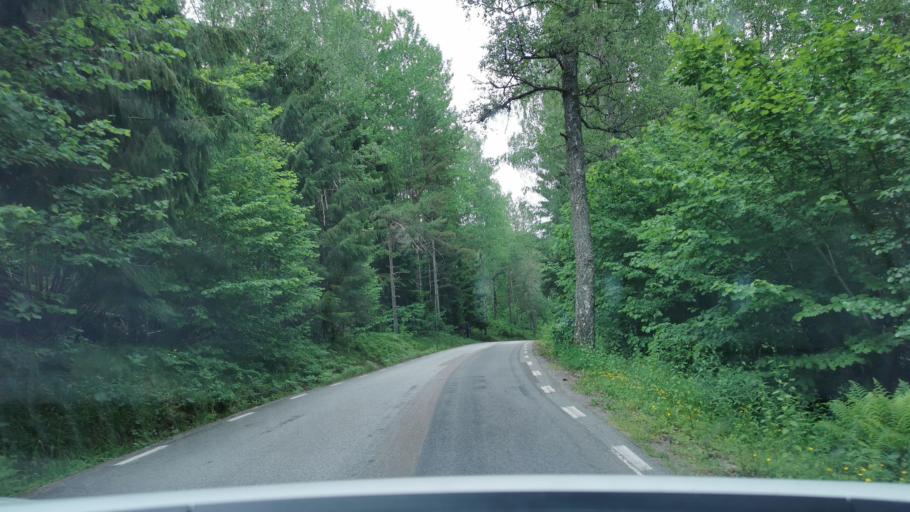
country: SE
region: Vaestra Goetaland
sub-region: Bengtsfors Kommun
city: Dals Langed
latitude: 58.8528
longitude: 12.4048
